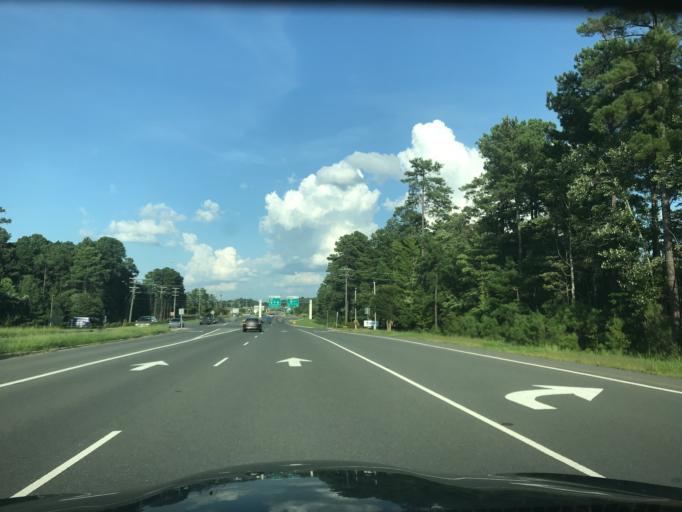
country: US
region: North Carolina
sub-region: Wake County
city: Morrisville
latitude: 35.8757
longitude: -78.8718
